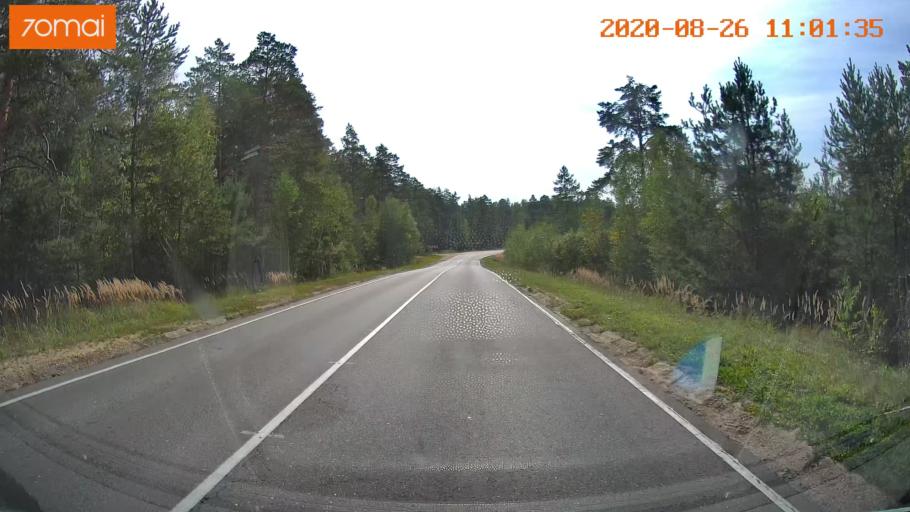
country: RU
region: Rjazan
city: Izhevskoye
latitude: 54.5611
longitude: 41.2262
